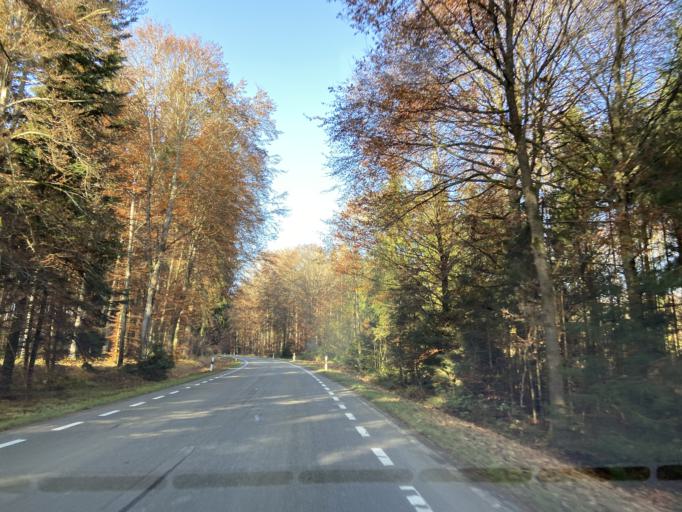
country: DE
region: Baden-Wuerttemberg
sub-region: Tuebingen Region
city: Sigmaringendorf
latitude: 48.0481
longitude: 9.2720
